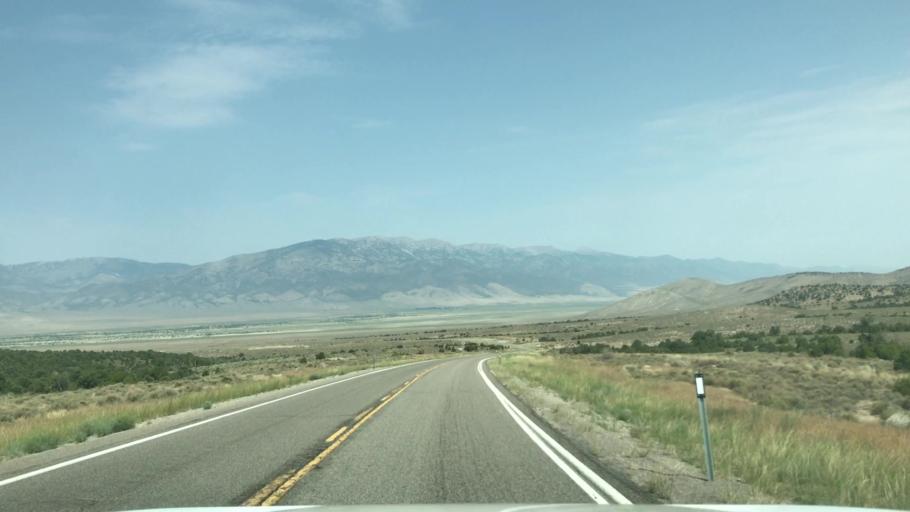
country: US
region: Nevada
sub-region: White Pine County
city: McGill
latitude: 39.1666
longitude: -114.3647
